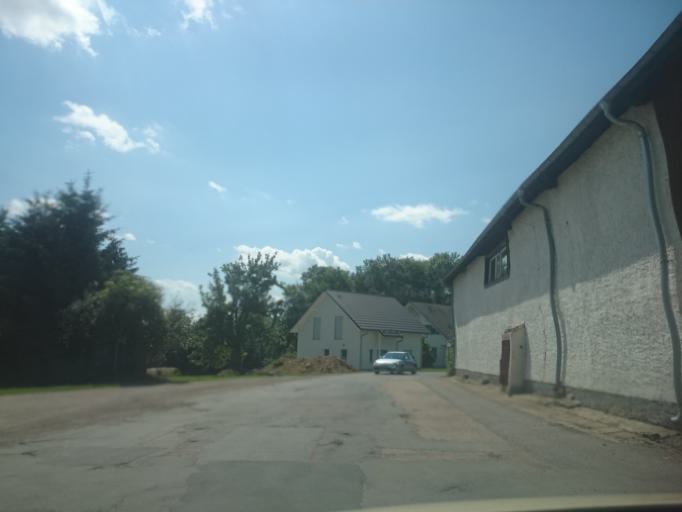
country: DE
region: Saxony
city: Brand-Erbisdorf
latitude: 50.8698
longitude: 13.3110
